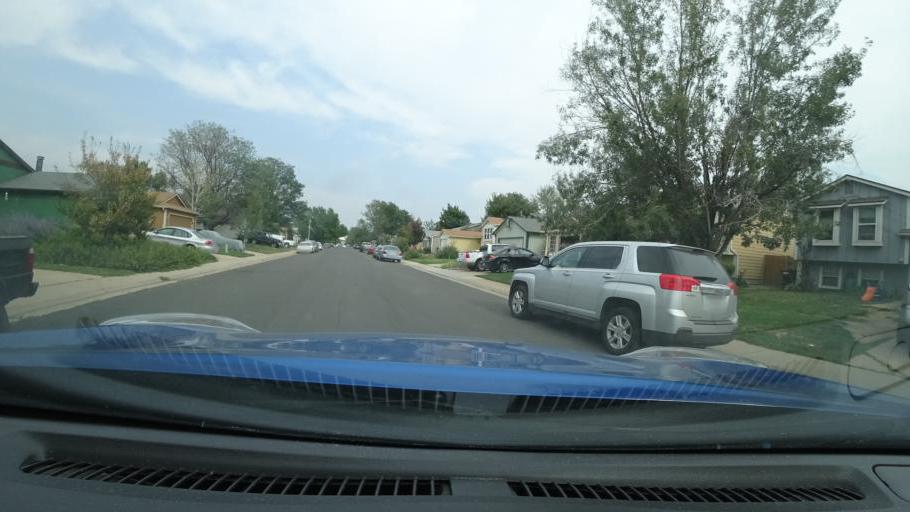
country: US
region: Colorado
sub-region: Adams County
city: Aurora
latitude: 39.7499
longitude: -104.7693
